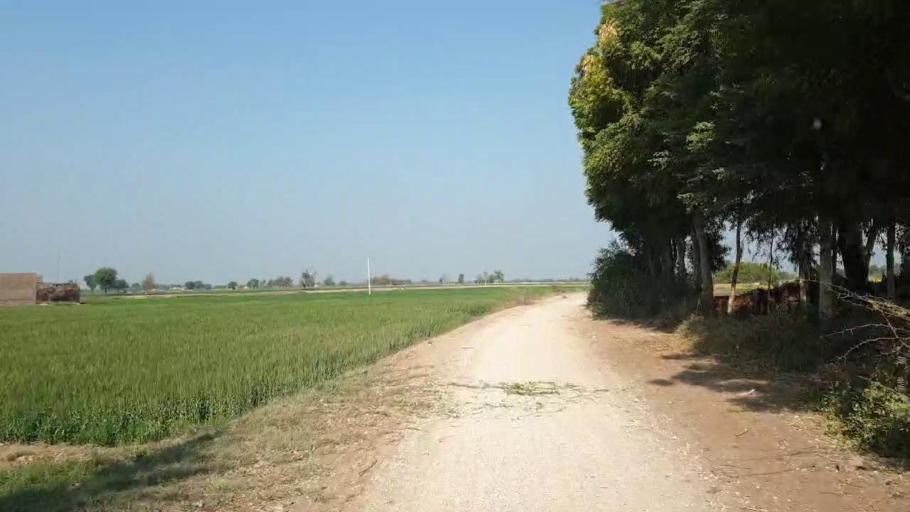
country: PK
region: Sindh
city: Hala
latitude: 25.9244
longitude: 68.4061
